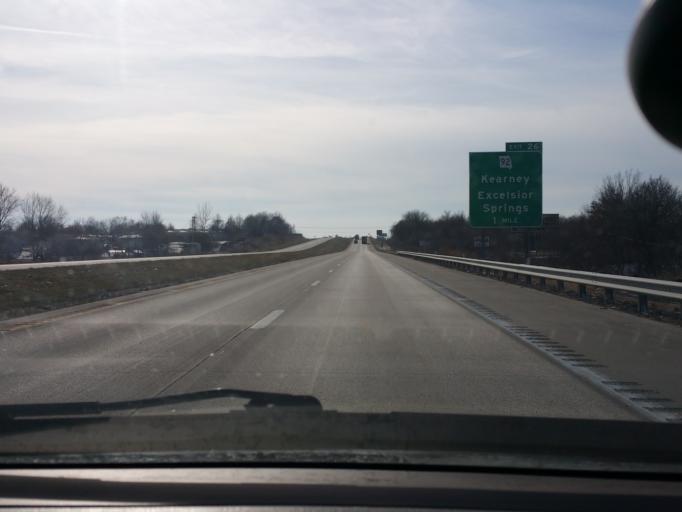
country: US
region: Missouri
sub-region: Clay County
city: Kearney
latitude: 39.3864
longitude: -94.3625
